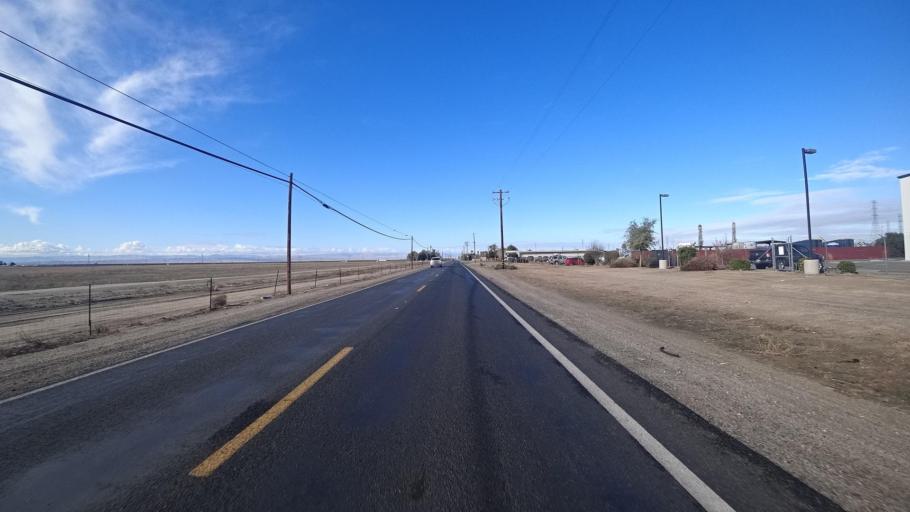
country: US
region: California
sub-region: Kern County
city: Rosedale
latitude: 35.3835
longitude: -119.2449
